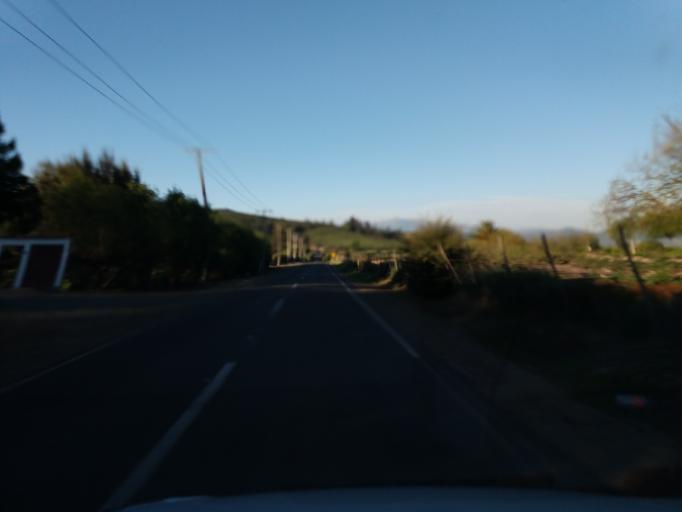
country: CL
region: Valparaiso
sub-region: Provincia de Quillota
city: Quillota
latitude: -32.9000
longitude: -71.2993
